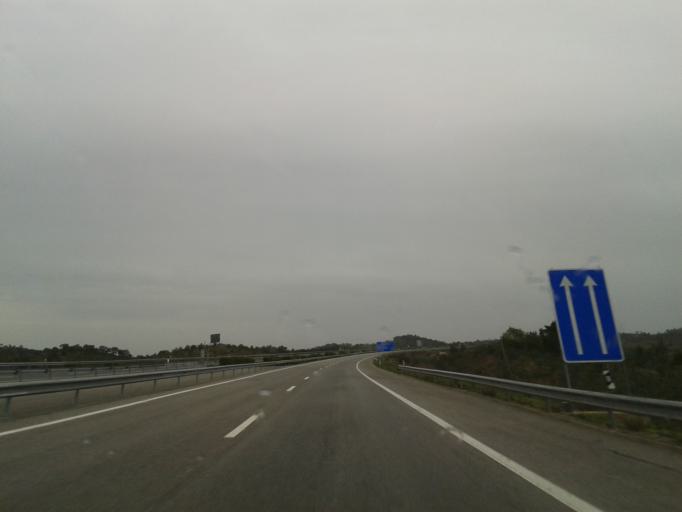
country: PT
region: Faro
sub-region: Silves
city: Sao Bartolomeu de Messines
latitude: 37.2591
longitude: -8.2580
